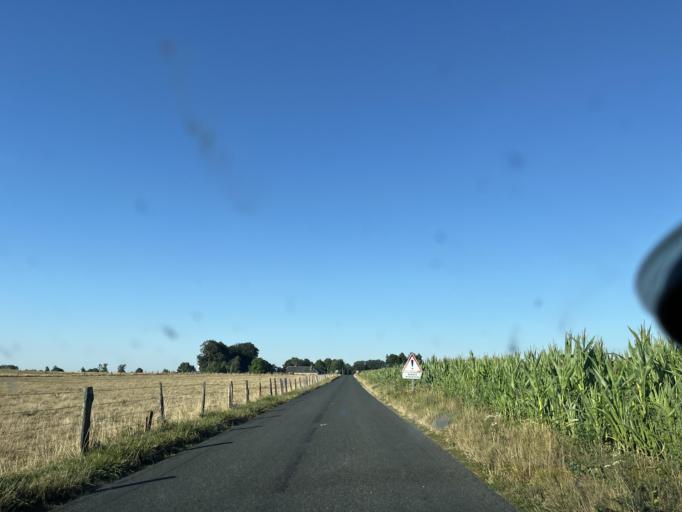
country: FR
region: Haute-Normandie
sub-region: Departement de la Seine-Maritime
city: Lanquetot
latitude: 49.5636
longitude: 0.5862
